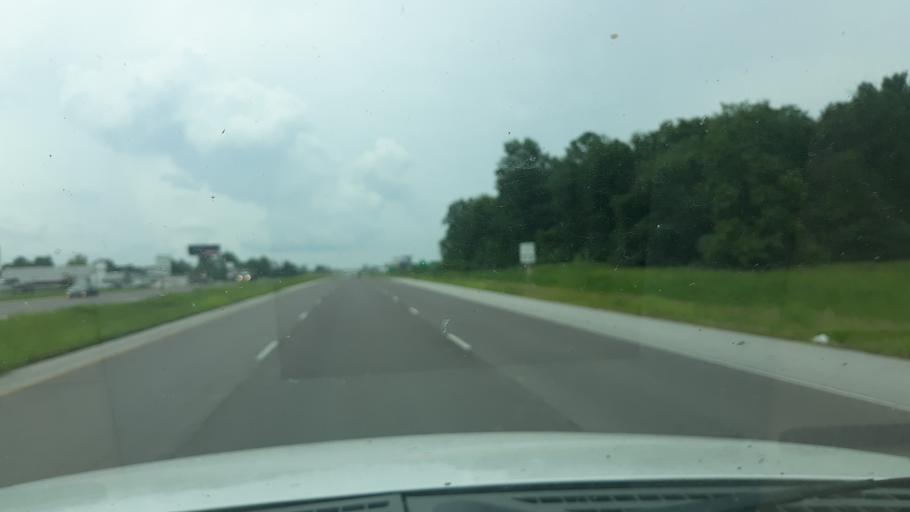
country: US
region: Illinois
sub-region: Williamson County
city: Crainville
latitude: 37.7450
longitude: -89.0736
